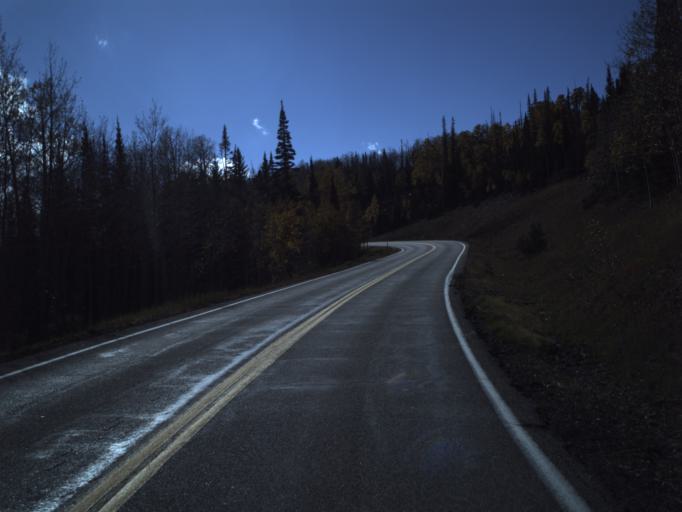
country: US
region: Utah
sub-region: Iron County
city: Parowan
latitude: 37.6561
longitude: -112.7523
